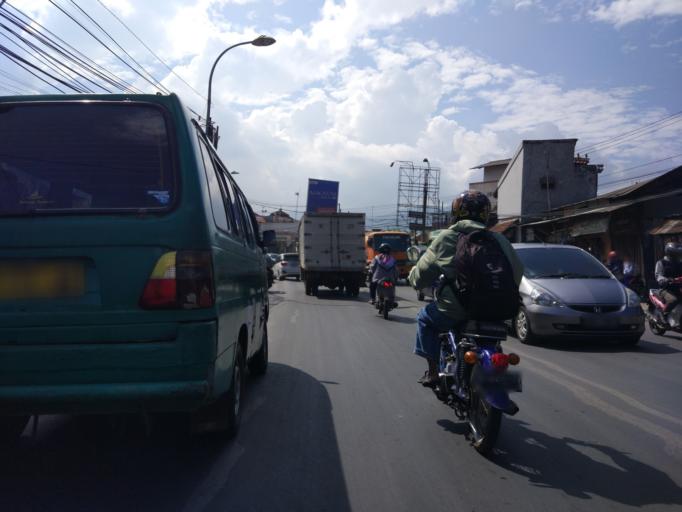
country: ID
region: West Java
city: Cileunyi
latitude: -6.9348
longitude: 107.7282
